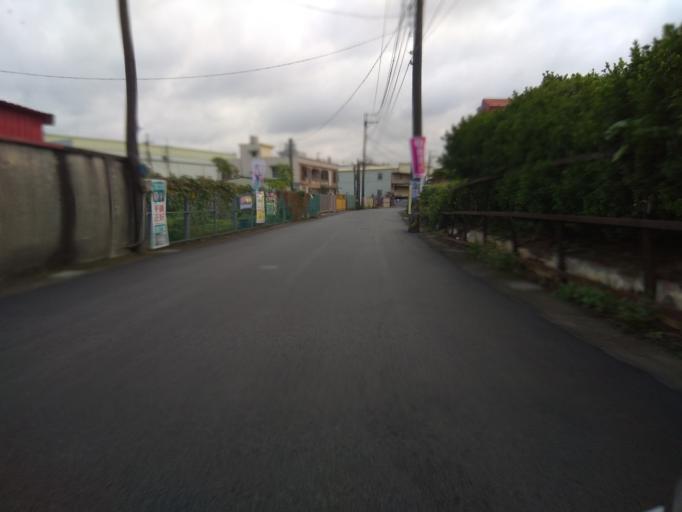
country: TW
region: Taiwan
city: Daxi
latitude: 24.9414
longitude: 121.1899
